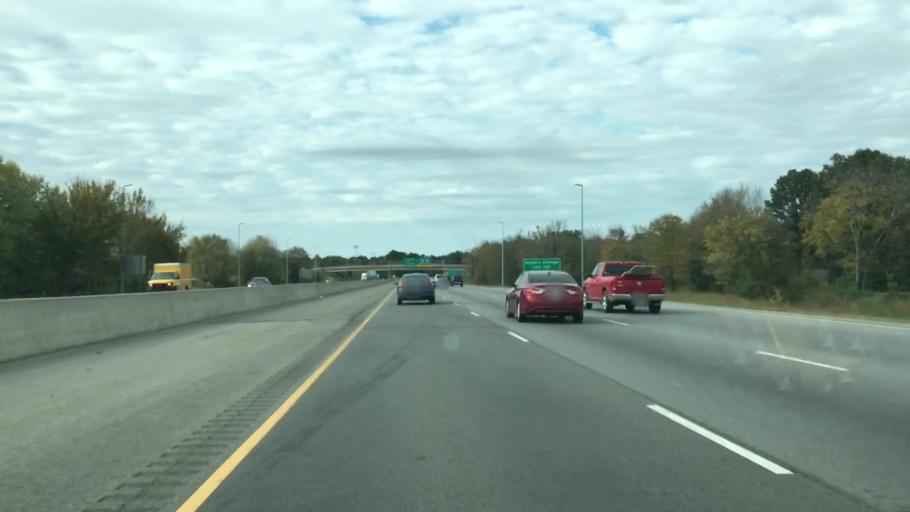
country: US
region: Arkansas
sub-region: Faulkner County
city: Conway
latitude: 35.0963
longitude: -92.4273
